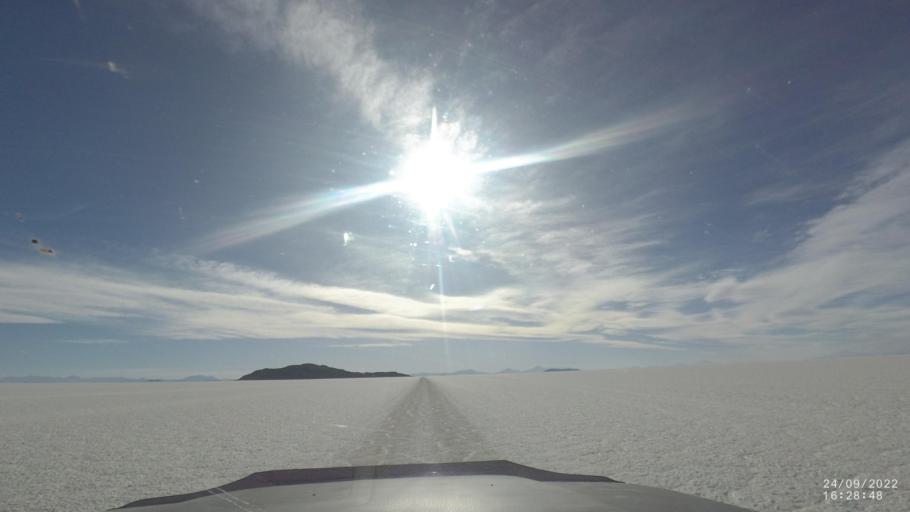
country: BO
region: Potosi
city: Colchani
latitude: -20.2413
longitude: -67.6049
